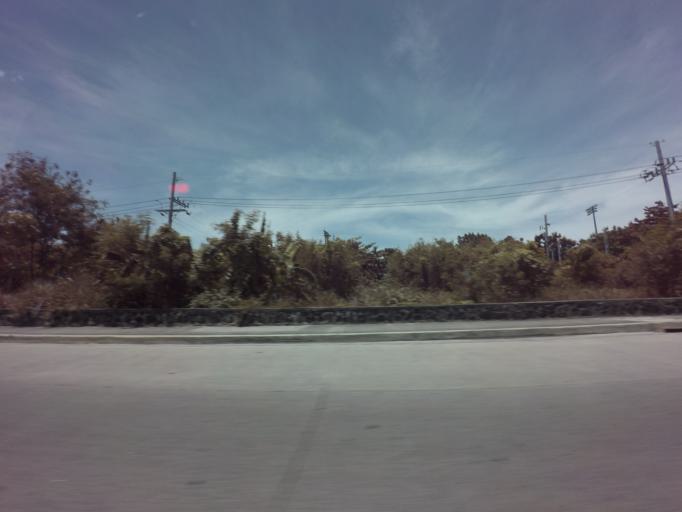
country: PH
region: Metro Manila
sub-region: Makati City
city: Makati City
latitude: 14.5025
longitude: 121.0196
